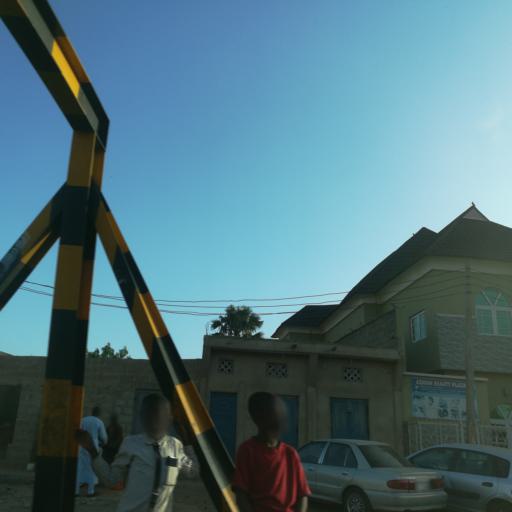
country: NG
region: Kano
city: Kano
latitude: 11.9909
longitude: 8.5301
